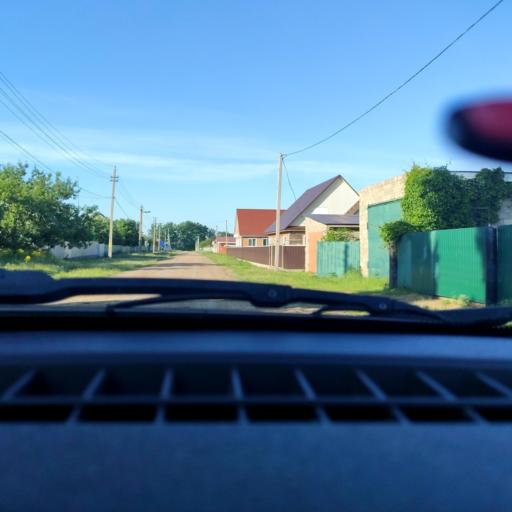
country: RU
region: Bashkortostan
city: Tolbazy
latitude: 54.2982
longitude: 55.8116
